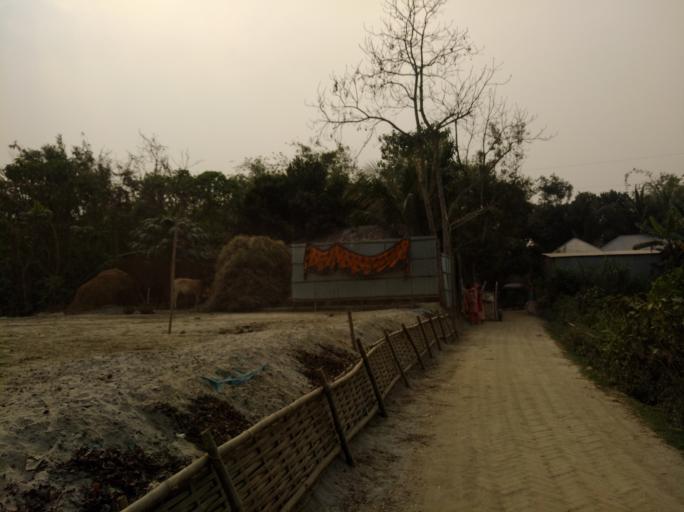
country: BD
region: Dhaka
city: Nagarpur
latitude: 24.0000
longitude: 89.8007
